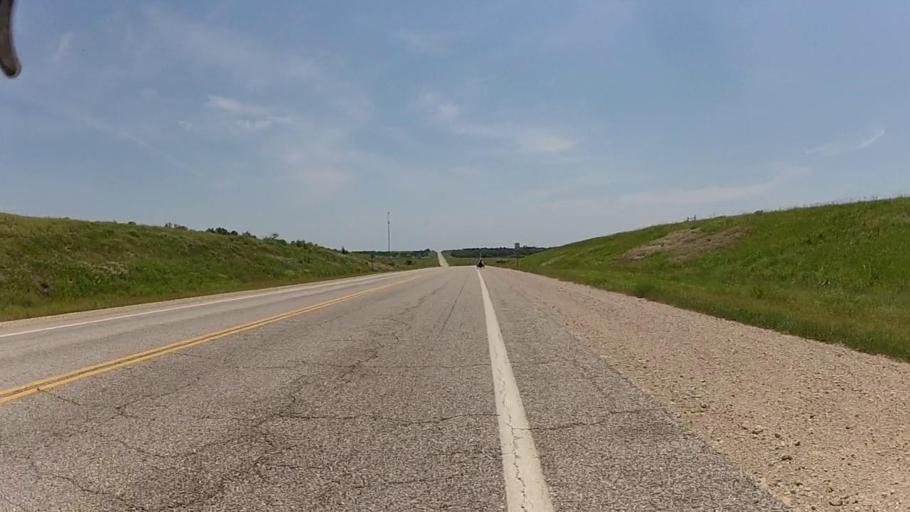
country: US
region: Kansas
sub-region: Chautauqua County
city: Sedan
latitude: 37.1134
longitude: -96.4647
